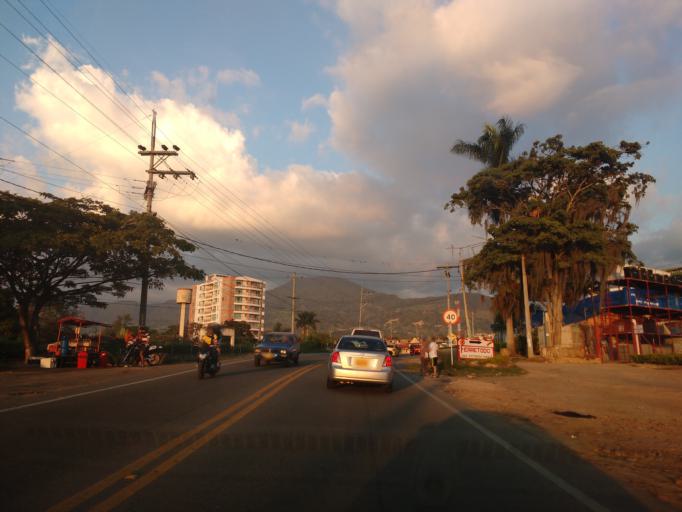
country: CO
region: Cundinamarca
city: Fusagasuga
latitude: 4.3300
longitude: -74.3809
